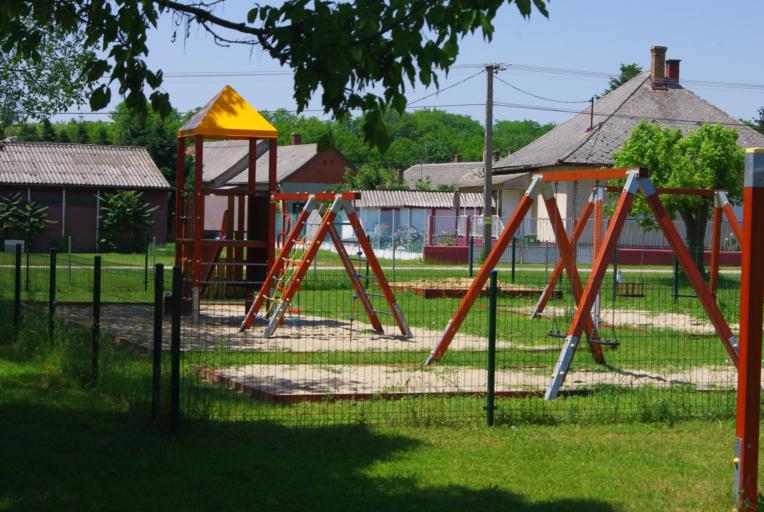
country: HU
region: Tolna
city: Bolcske
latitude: 46.7463
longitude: 18.9698
